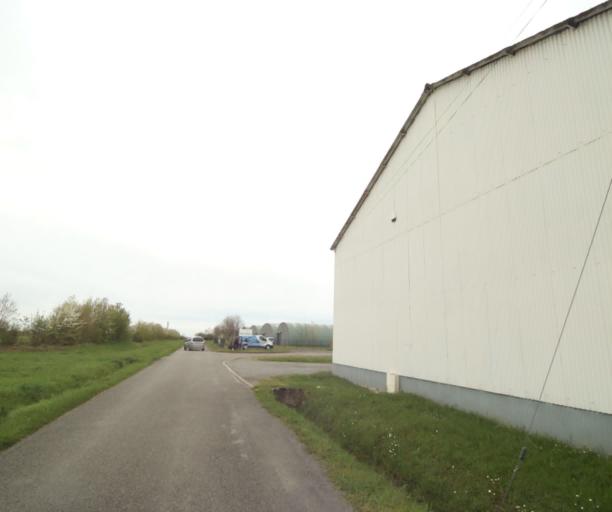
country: FR
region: Bourgogne
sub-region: Departement de Saone-et-Loire
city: Charnay-les-Macon
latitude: 46.2944
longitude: 4.7992
